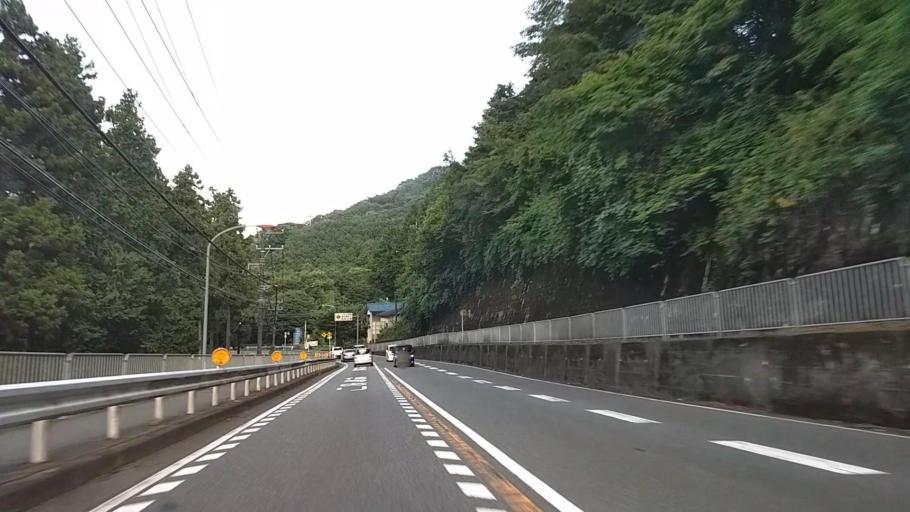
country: JP
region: Tokyo
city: Hachioji
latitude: 35.5877
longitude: 139.2401
